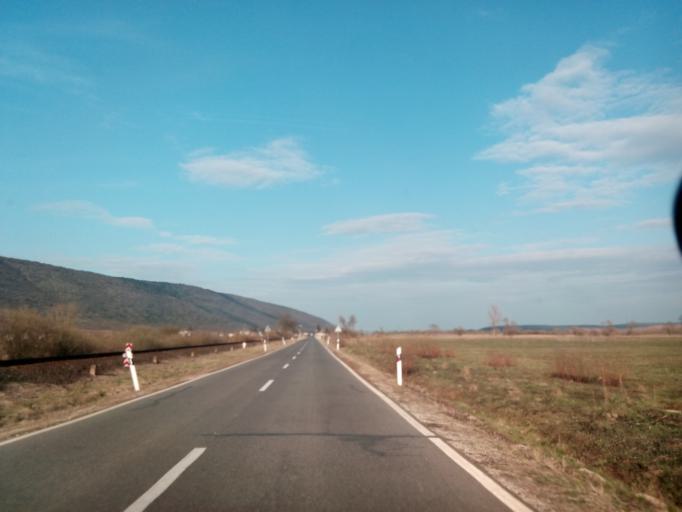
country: HU
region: Borsod-Abauj-Zemplen
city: Szendro
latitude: 48.5533
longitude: 20.7752
